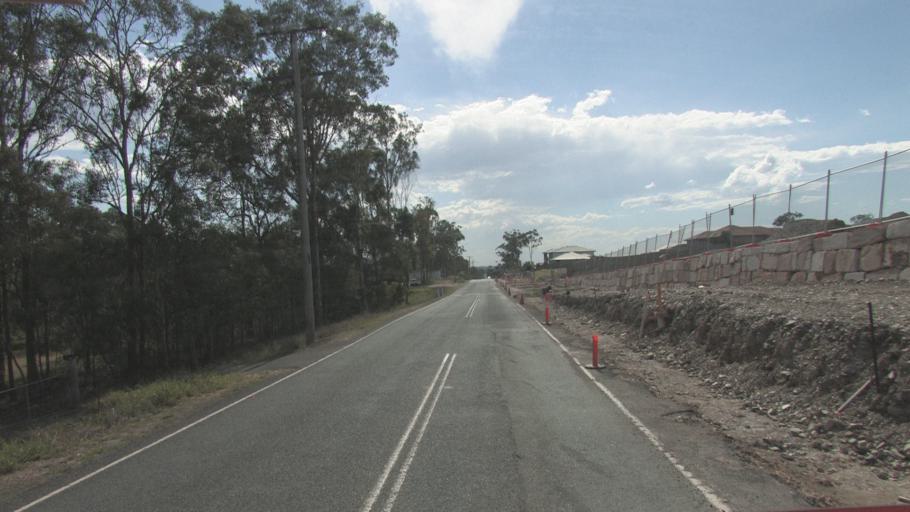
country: AU
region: Queensland
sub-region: Logan
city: Waterford West
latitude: -27.7204
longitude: 153.1574
